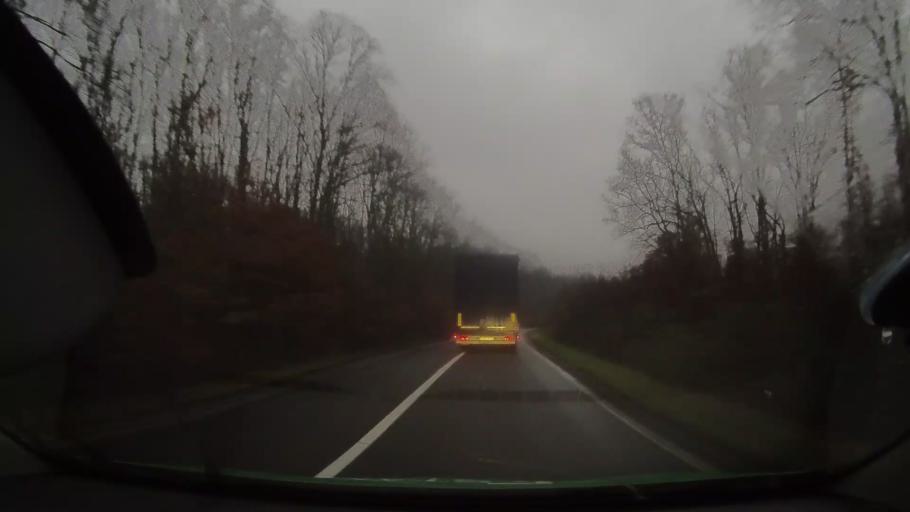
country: RO
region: Arad
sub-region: Comuna Beliu
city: Beliu
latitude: 46.5105
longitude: 21.9643
